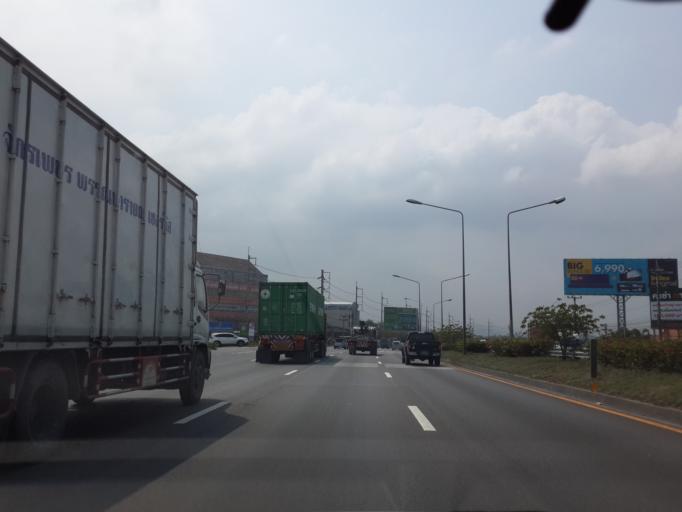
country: TH
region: Chon Buri
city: Chon Buri
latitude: 13.3659
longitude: 101.0182
